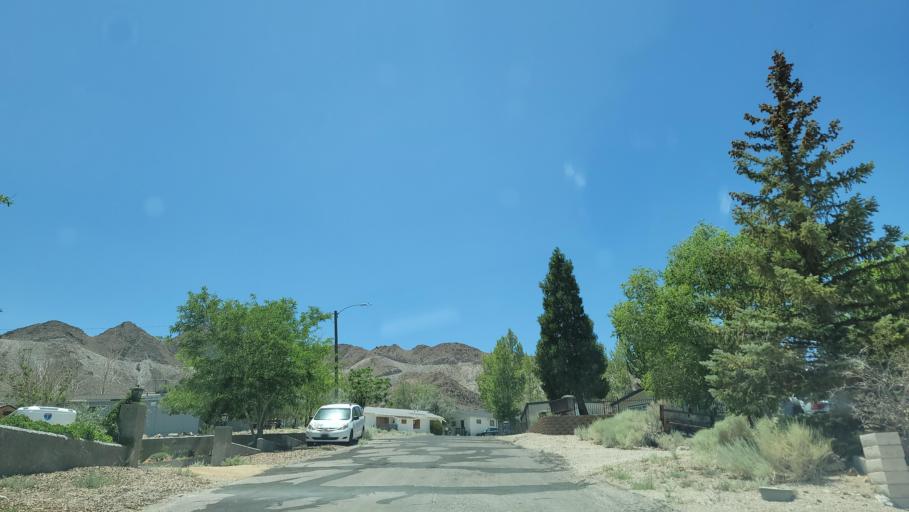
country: US
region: Nevada
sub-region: Nye County
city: Tonopah
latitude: 38.0605
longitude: -117.2307
